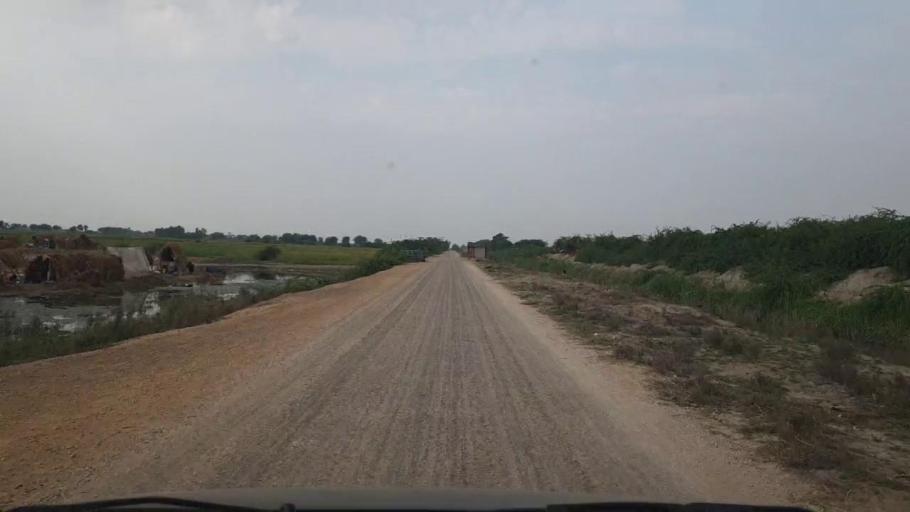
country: PK
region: Sindh
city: Kario
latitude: 24.6022
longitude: 68.6011
